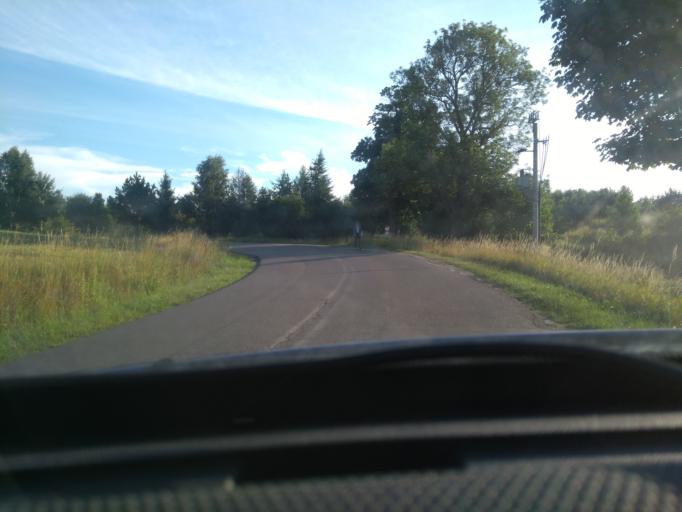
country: PL
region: Pomeranian Voivodeship
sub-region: Powiat kartuski
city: Przodkowo
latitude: 54.3946
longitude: 18.3411
